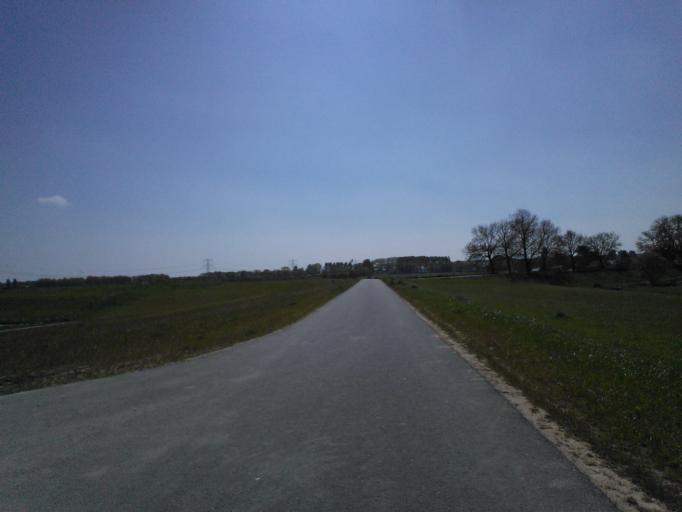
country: NL
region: South Holland
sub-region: Gemeente Sliedrecht
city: Sliedrecht
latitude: 51.7979
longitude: 4.7396
